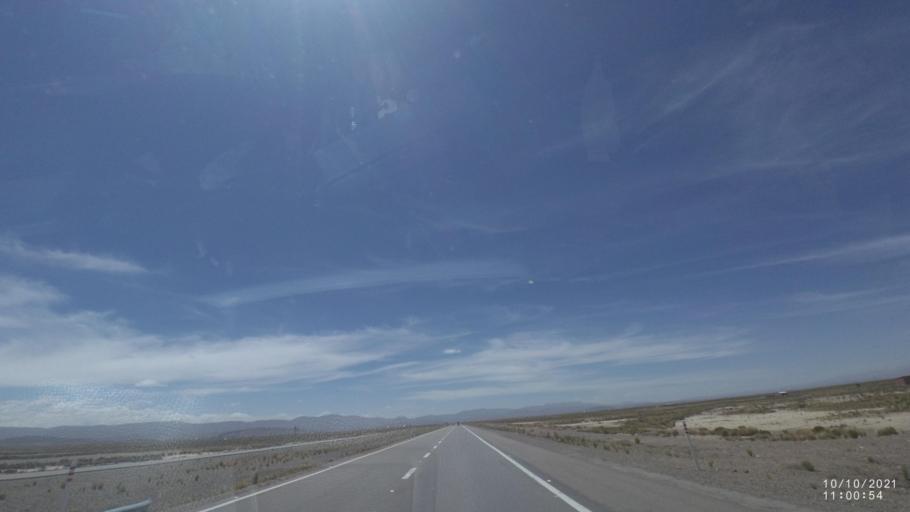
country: BO
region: La Paz
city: Colquiri
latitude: -17.6491
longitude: -67.1916
